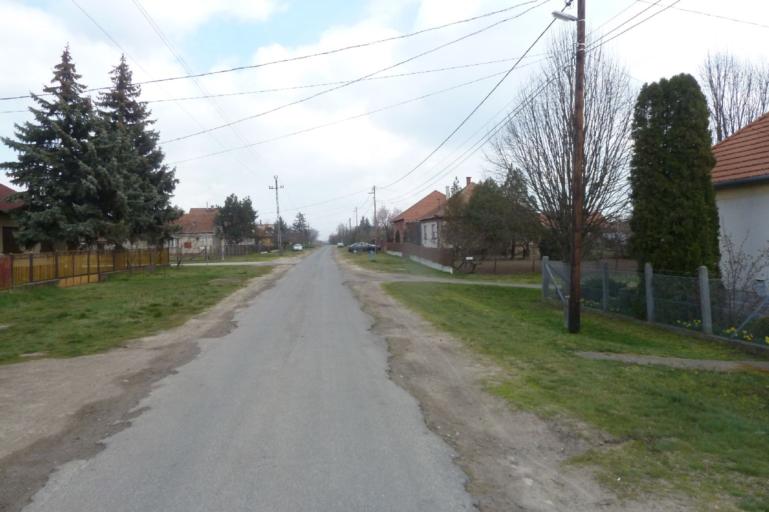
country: HU
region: Pest
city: Tapioszele
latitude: 47.3386
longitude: 19.8804
